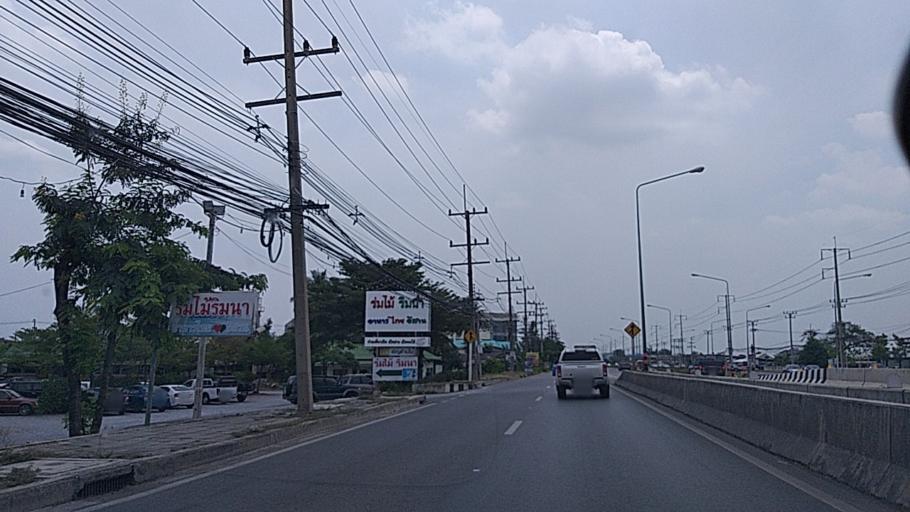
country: TH
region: Nakhon Pathom
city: Salaya
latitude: 13.7838
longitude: 100.3028
